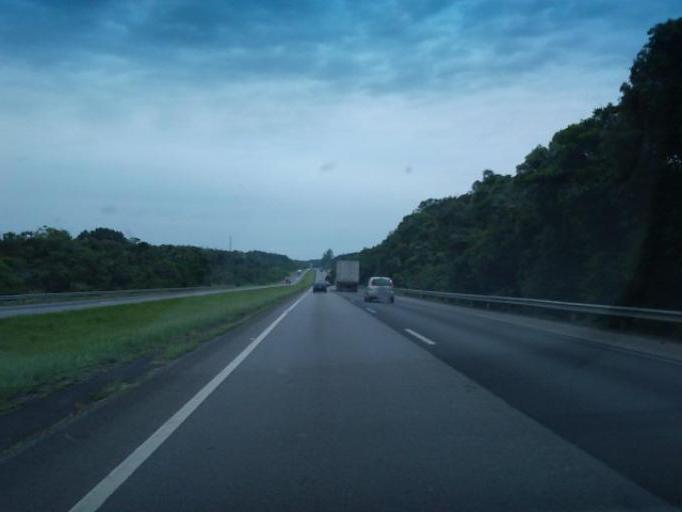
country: BR
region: Sao Paulo
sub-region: Registro
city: Registro
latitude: -24.5442
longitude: -47.8616
